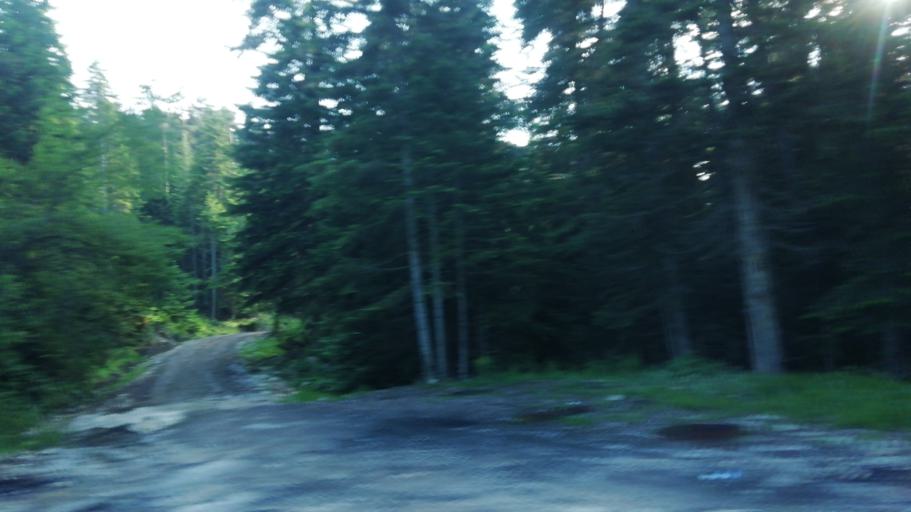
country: TR
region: Karabuk
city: Eskipazar
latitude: 41.0508
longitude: 32.5408
